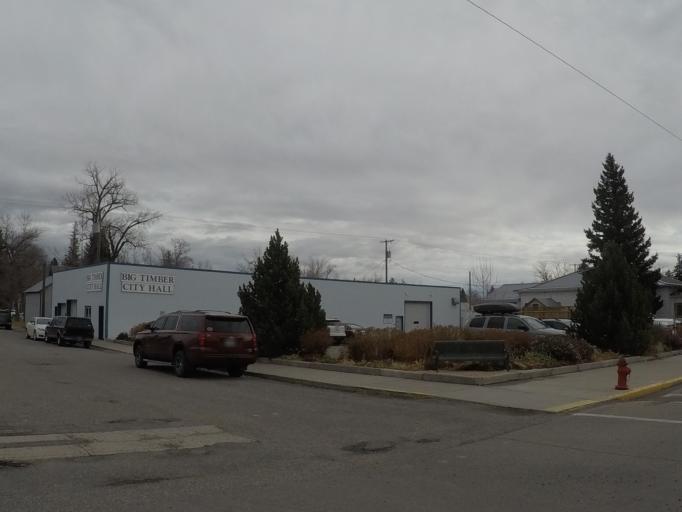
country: US
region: Montana
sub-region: Sweet Grass County
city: Big Timber
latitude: 45.8334
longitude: -109.9535
